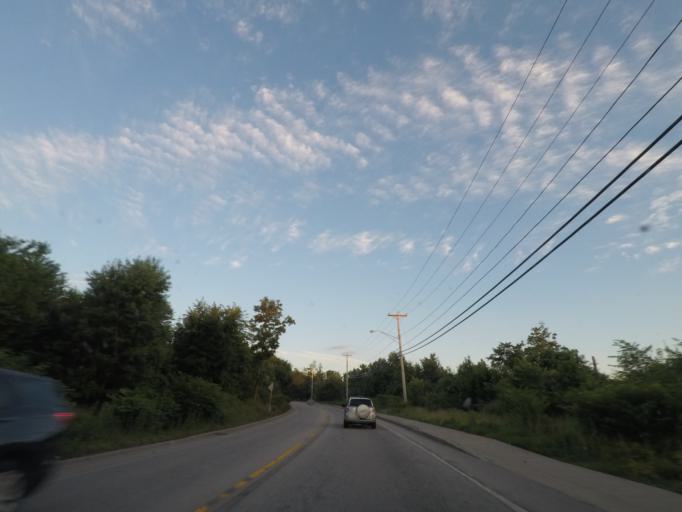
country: US
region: Massachusetts
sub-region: Worcester County
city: Sturbridge
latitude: 42.1020
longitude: -72.0757
